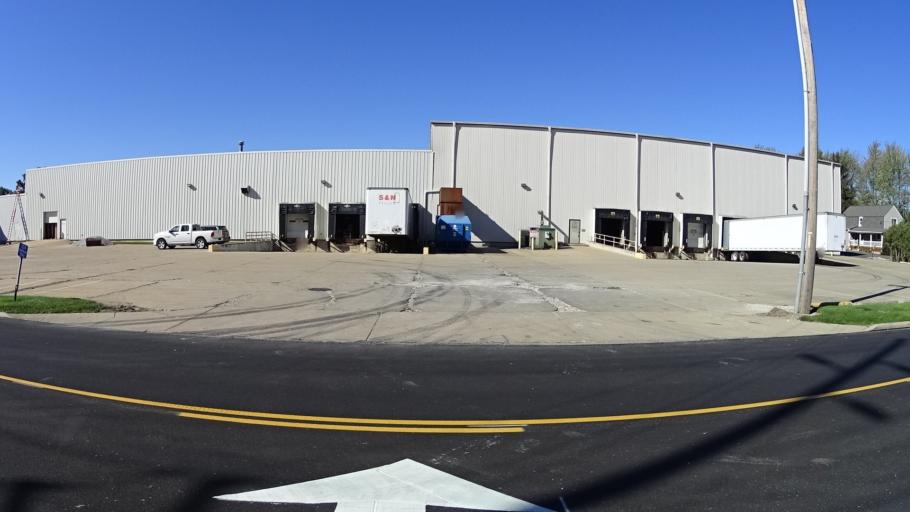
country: US
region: Ohio
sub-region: Lorain County
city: Oberlin
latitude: 41.2953
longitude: -82.1971
